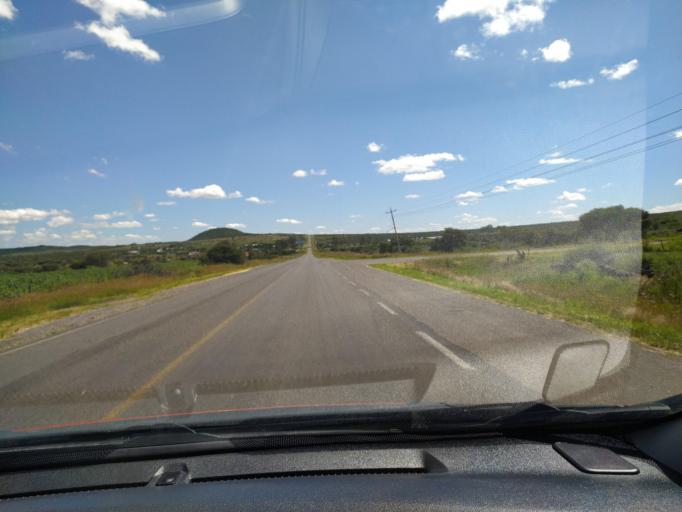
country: MX
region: Jalisco
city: San Miguel el Alto
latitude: 21.0193
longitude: -102.4580
